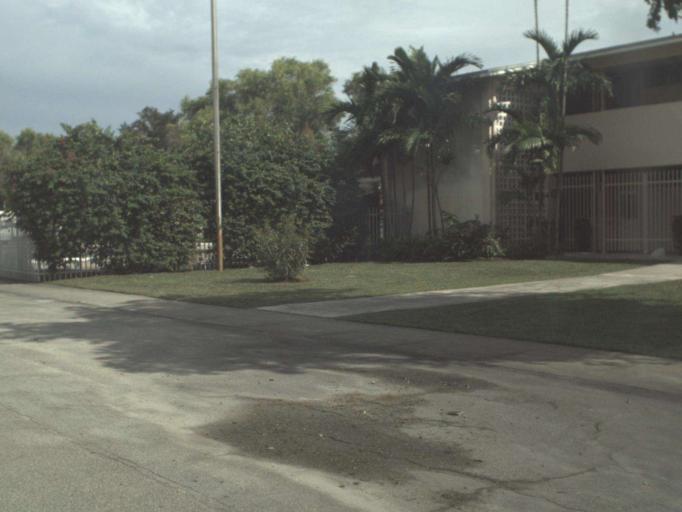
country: US
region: Florida
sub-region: Miami-Dade County
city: North Miami
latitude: 25.8843
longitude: -80.1978
